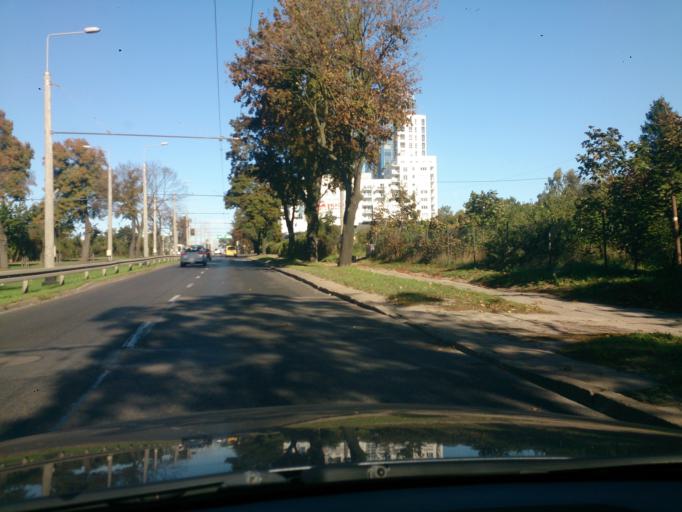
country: PL
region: Pomeranian Voivodeship
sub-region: Gdynia
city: Gdynia
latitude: 54.4888
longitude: 18.5432
